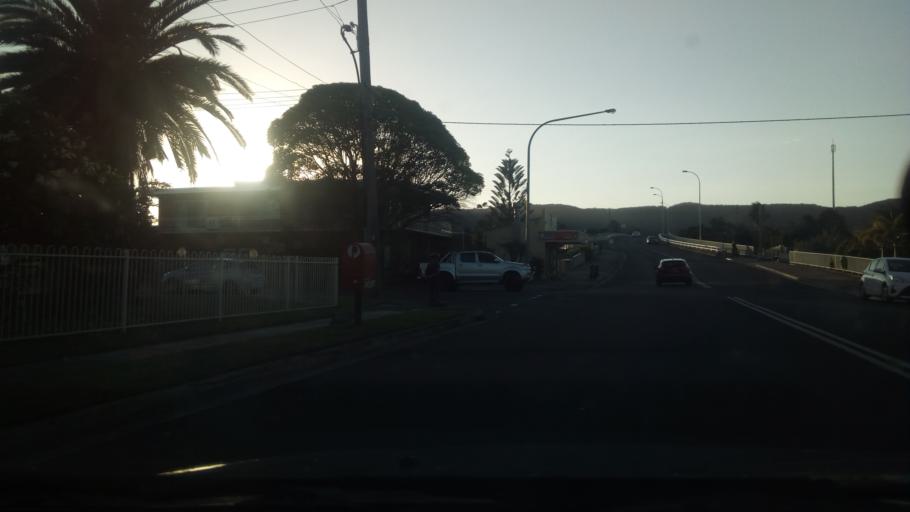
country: AU
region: New South Wales
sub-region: Wollongong
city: Fairy Meadow
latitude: -34.3955
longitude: 150.8987
